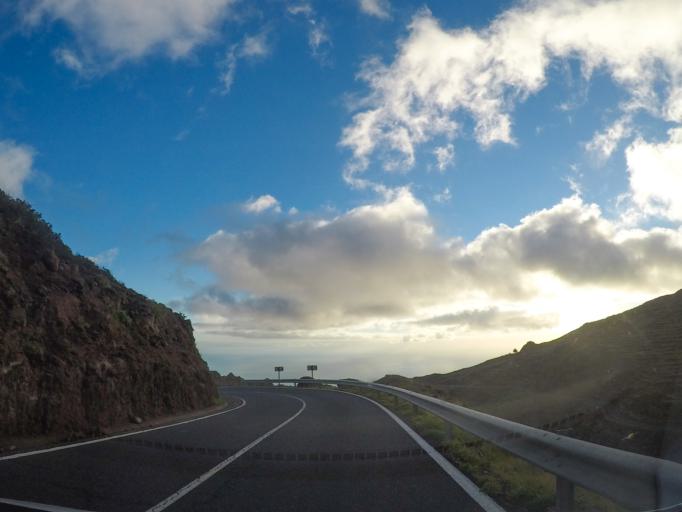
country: ES
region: Canary Islands
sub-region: Provincia de Santa Cruz de Tenerife
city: Alajero
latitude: 28.0824
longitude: -17.2461
